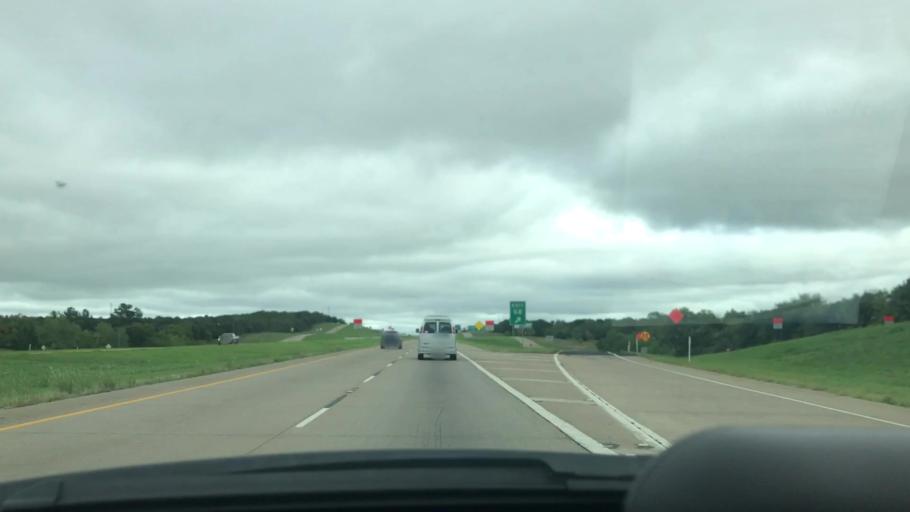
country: US
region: Texas
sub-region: Grayson County
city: Denison
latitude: 33.7443
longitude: -96.5852
